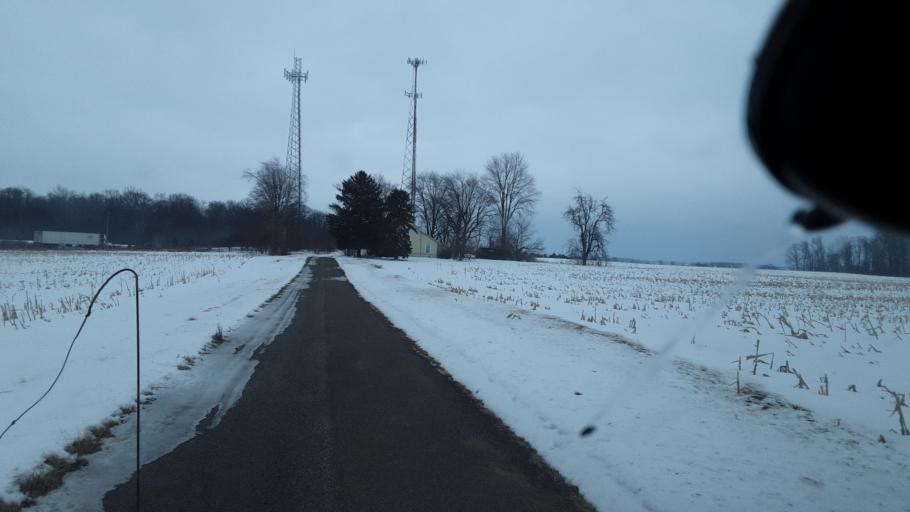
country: US
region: Ohio
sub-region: Union County
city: New California
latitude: 40.1971
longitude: -83.2802
